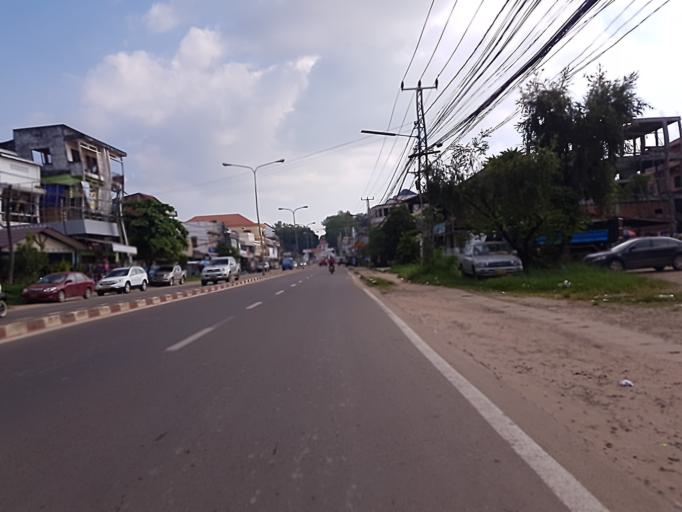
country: TH
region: Nong Khai
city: Si Chiang Mai
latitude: 17.9119
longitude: 102.6203
